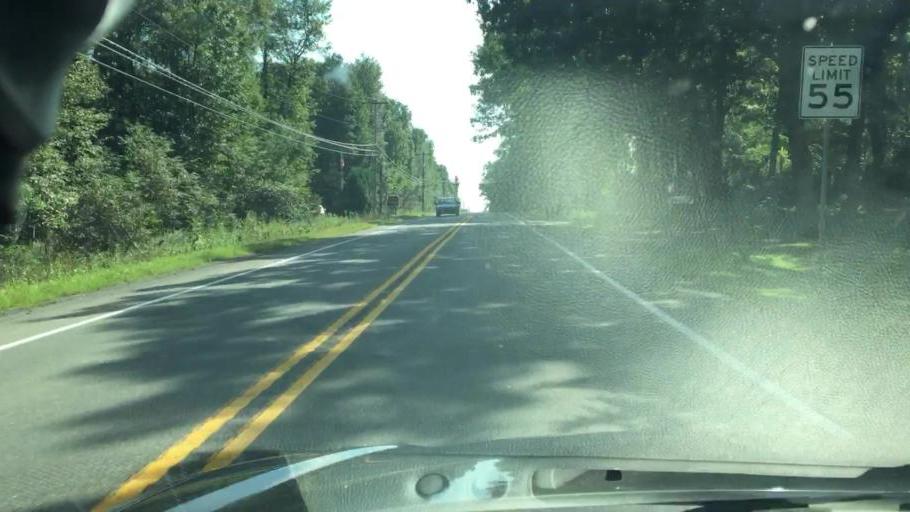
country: US
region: Pennsylvania
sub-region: Carbon County
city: Towamensing Trails
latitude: 40.9779
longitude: -75.6356
